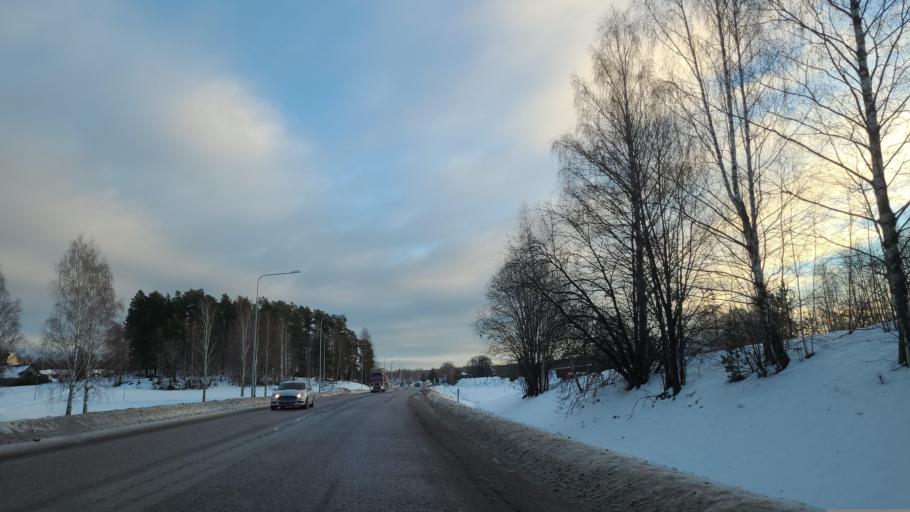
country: SE
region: Gaevleborg
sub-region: Bollnas Kommun
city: Bollnas
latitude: 61.3566
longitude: 16.4158
